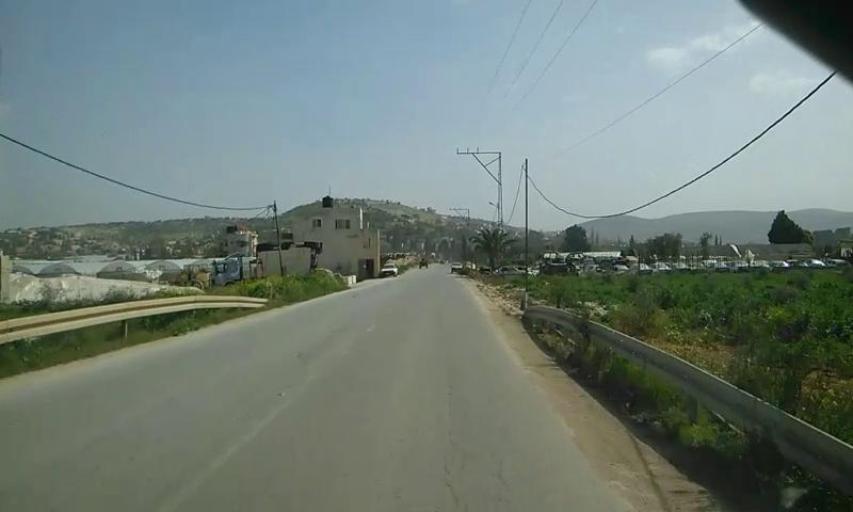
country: PS
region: West Bank
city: Ash Shuhada'
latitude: 32.4334
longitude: 35.2664
